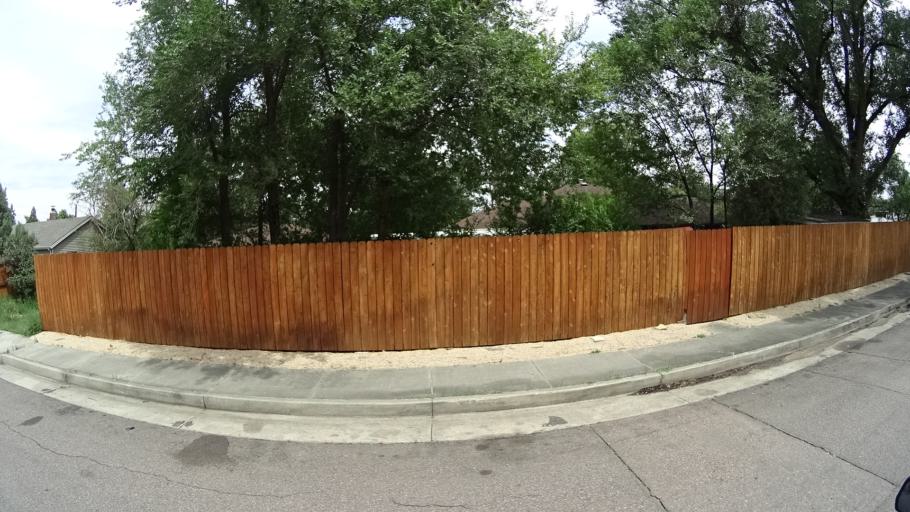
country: US
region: Colorado
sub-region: El Paso County
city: Colorado Springs
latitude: 38.8525
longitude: -104.8349
